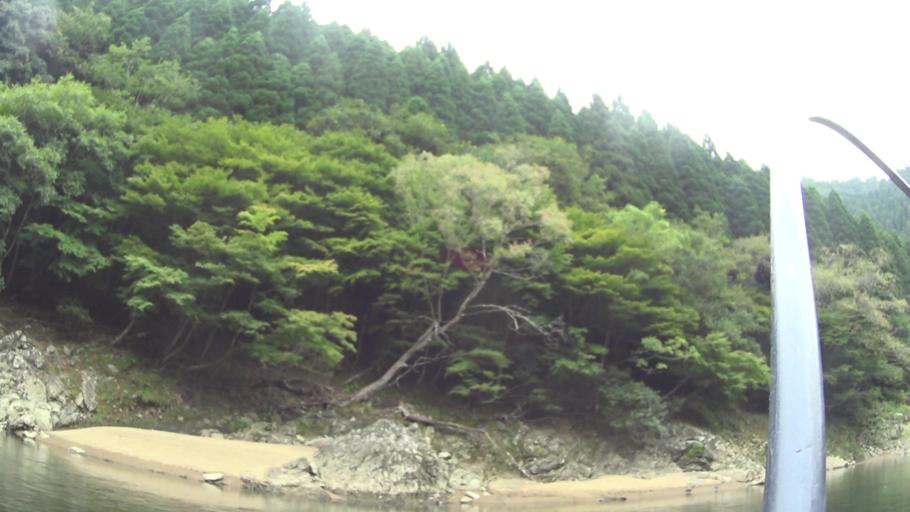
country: JP
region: Kyoto
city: Kameoka
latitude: 35.0232
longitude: 135.6267
